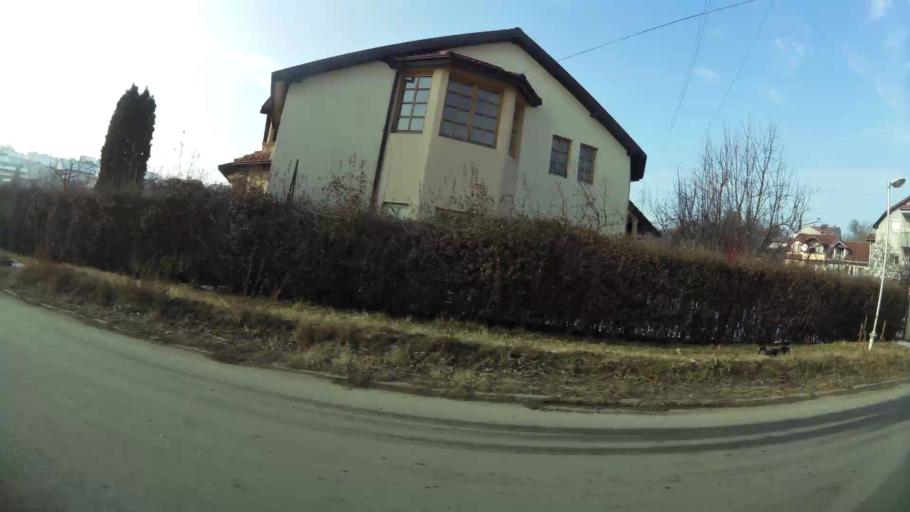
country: MK
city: Creshevo
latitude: 42.0106
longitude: 21.5014
